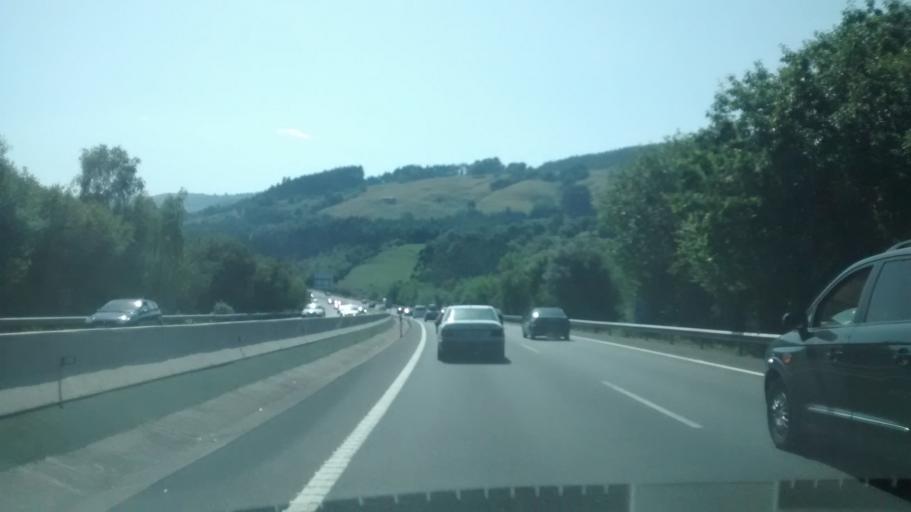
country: ES
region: Cantabria
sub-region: Provincia de Cantabria
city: Laredo
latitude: 43.3944
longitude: -3.3976
